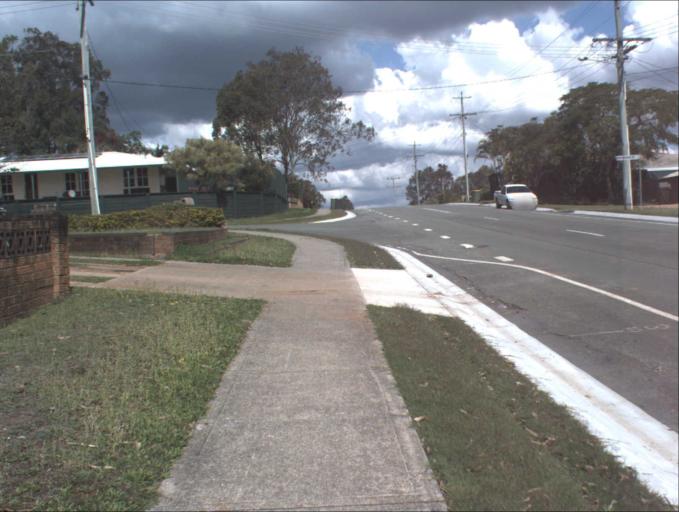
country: AU
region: Queensland
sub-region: Logan
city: Waterford West
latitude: -27.6921
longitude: 153.1511
